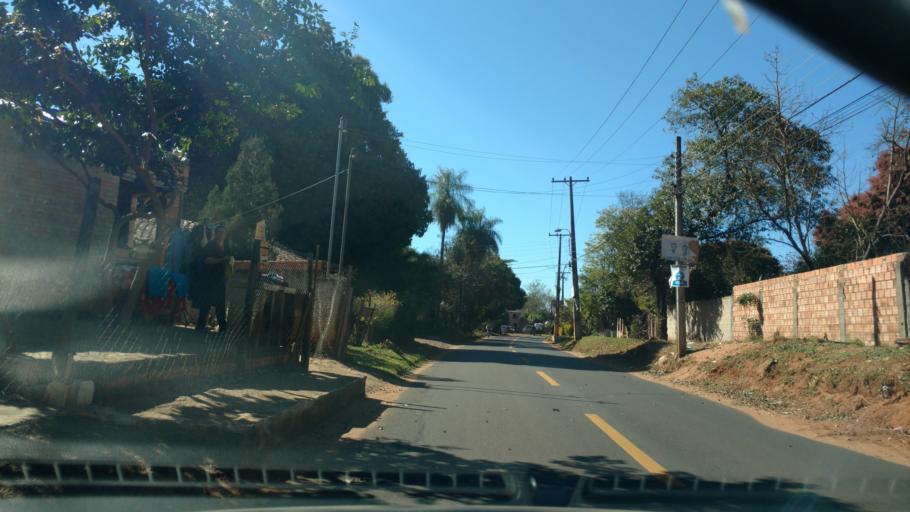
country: PY
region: Central
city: Capiata
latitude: -25.3607
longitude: -57.4166
